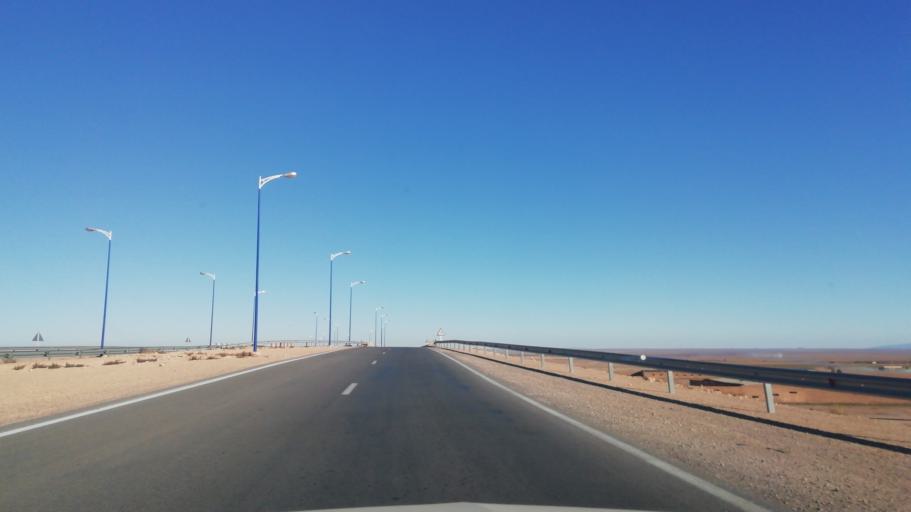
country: DZ
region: Wilaya de Naama
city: Naama
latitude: 33.5126
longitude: -0.2823
